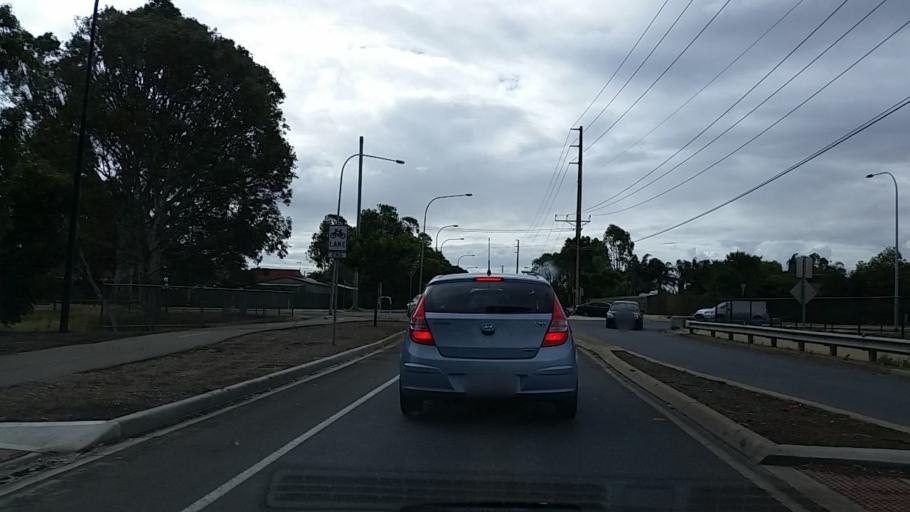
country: AU
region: South Australia
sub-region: Playford
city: Smithfield
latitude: -34.6697
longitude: 138.6740
